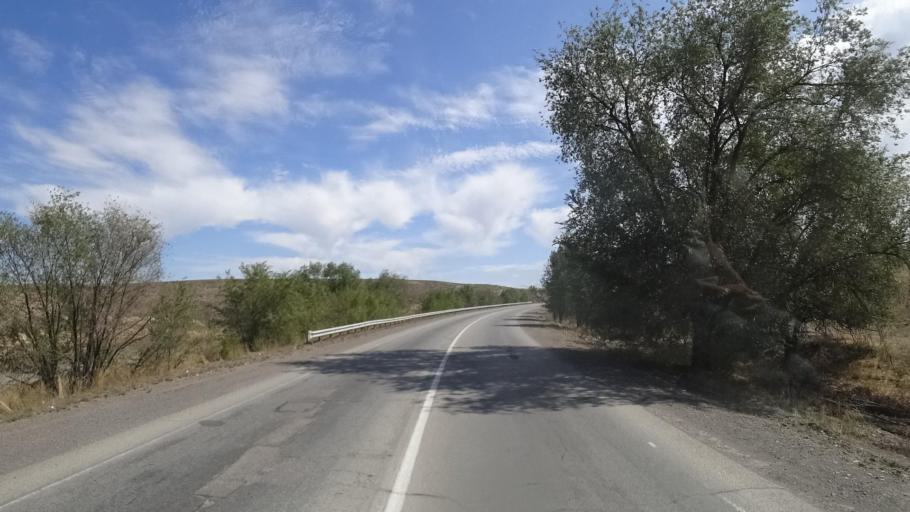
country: KZ
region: Almaty Oblysy
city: Burunday
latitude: 43.3144
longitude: 76.1732
